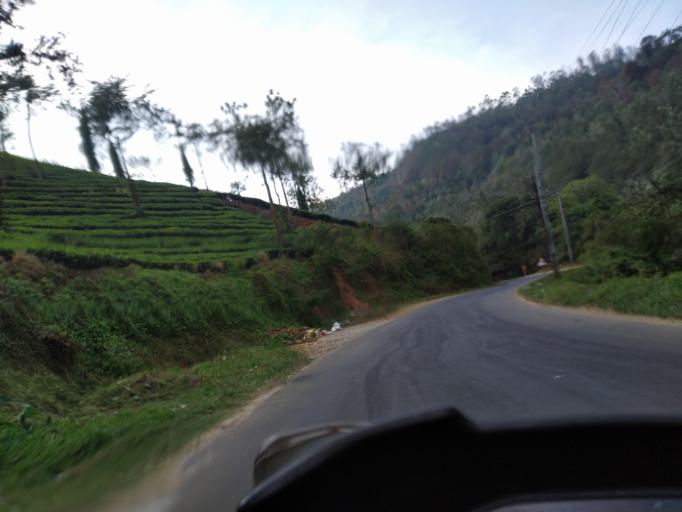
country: IN
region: Tamil Nadu
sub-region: Theni
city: Gudalur
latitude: 9.5949
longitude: 77.1254
